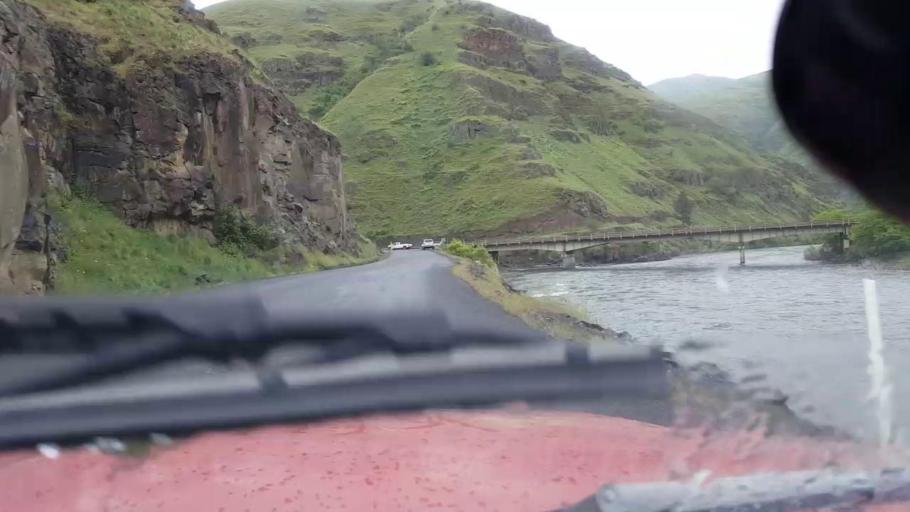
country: US
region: Washington
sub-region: Asotin County
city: Asotin
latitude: 46.0429
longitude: -117.2534
